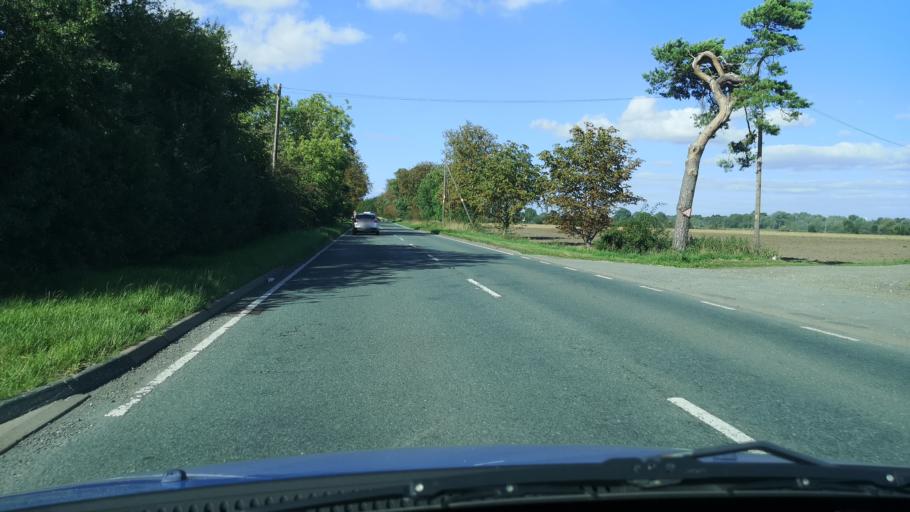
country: GB
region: England
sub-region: North Lincolnshire
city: Belton
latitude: 53.5733
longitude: -0.8177
